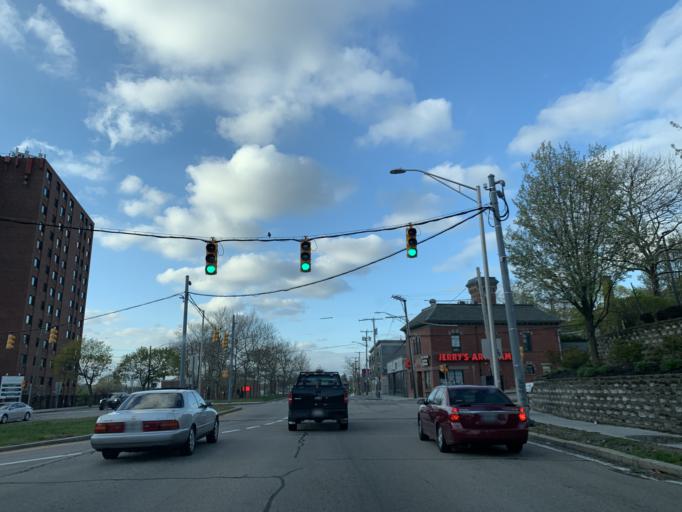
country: US
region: Rhode Island
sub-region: Providence County
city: Providence
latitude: 41.8380
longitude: -71.4093
